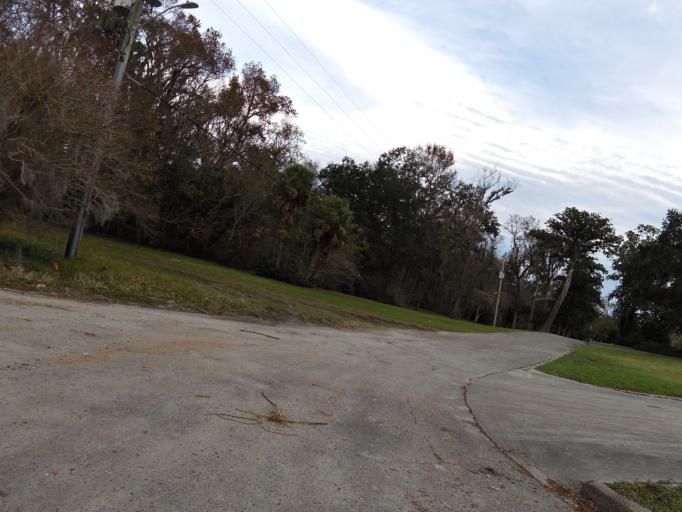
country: US
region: Florida
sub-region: Duval County
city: Jacksonville
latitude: 30.2458
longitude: -81.6355
